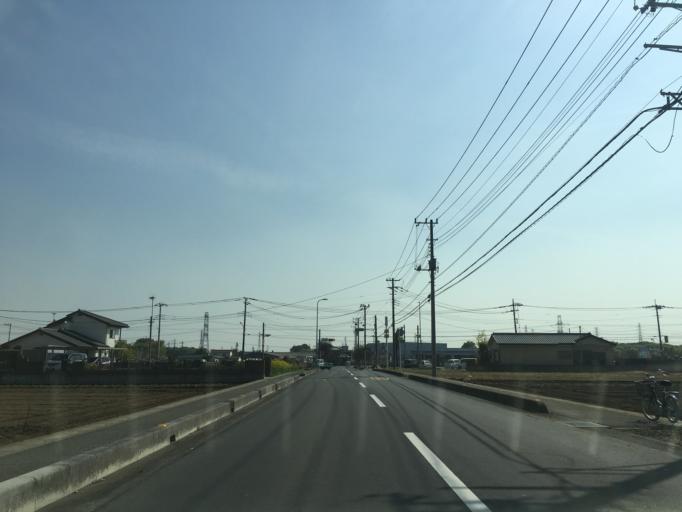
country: JP
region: Saitama
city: Sugito
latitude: 36.0074
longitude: 139.7199
